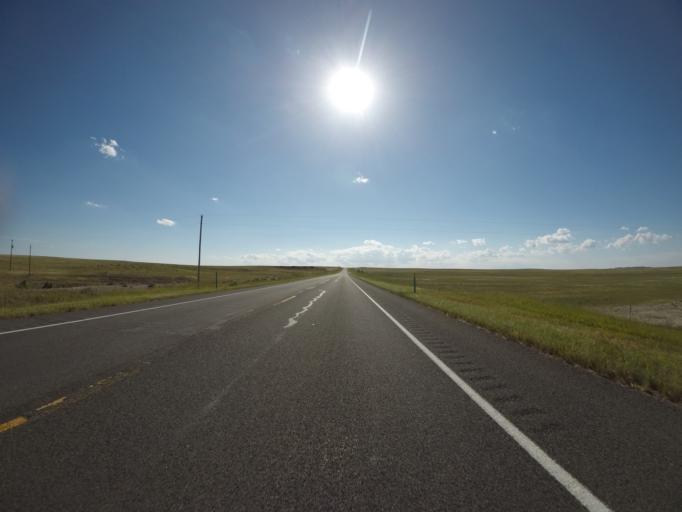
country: US
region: Colorado
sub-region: Morgan County
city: Brush
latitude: 40.6108
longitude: -103.5798
